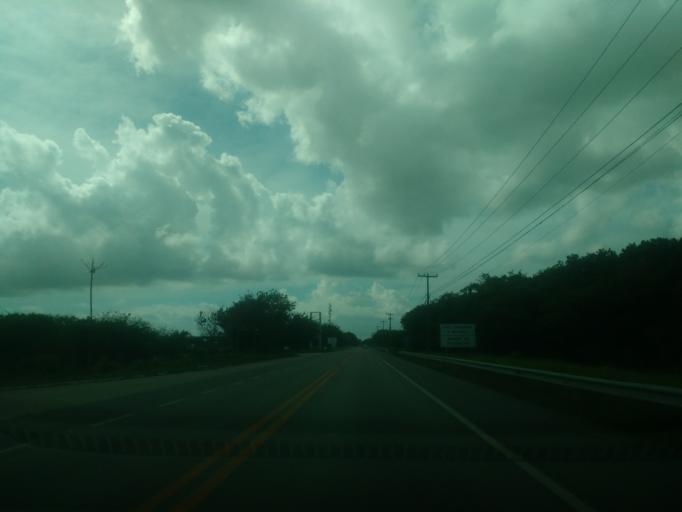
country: BR
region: Alagoas
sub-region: Marechal Deodoro
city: Marechal Deodoro
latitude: -9.6698
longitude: -35.8419
